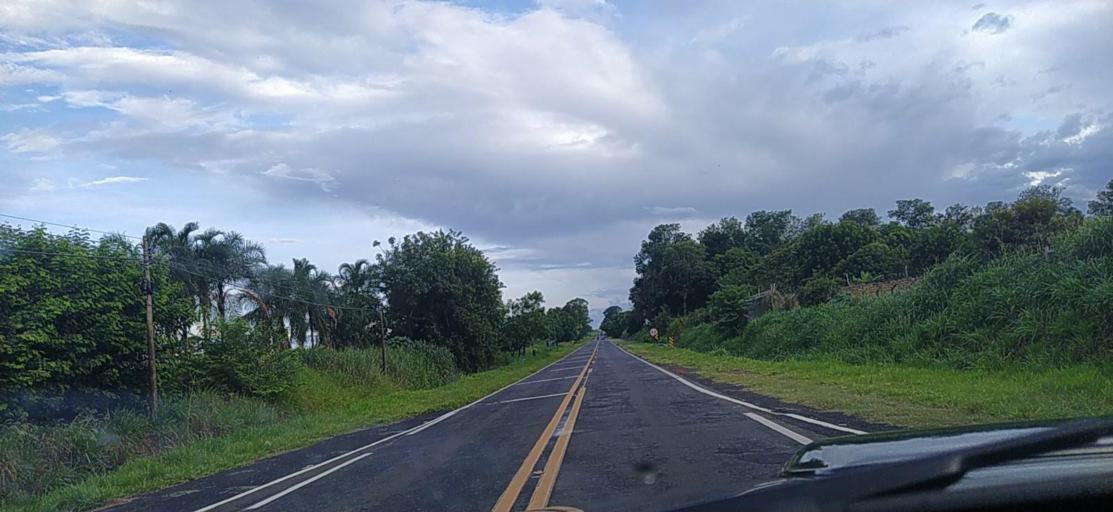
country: BR
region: Sao Paulo
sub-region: Catanduva
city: Catanduva
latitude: -21.1623
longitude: -48.9424
